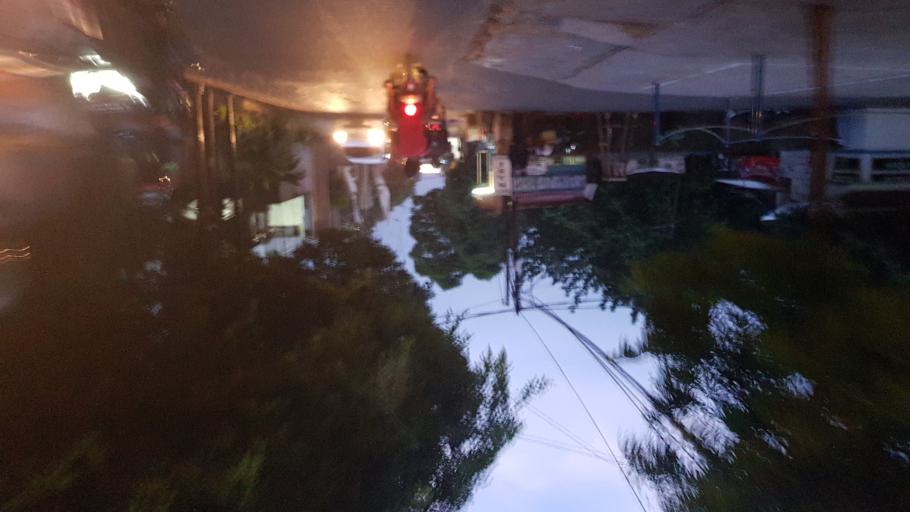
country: ID
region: West Java
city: Depok
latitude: -6.3443
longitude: 106.8030
